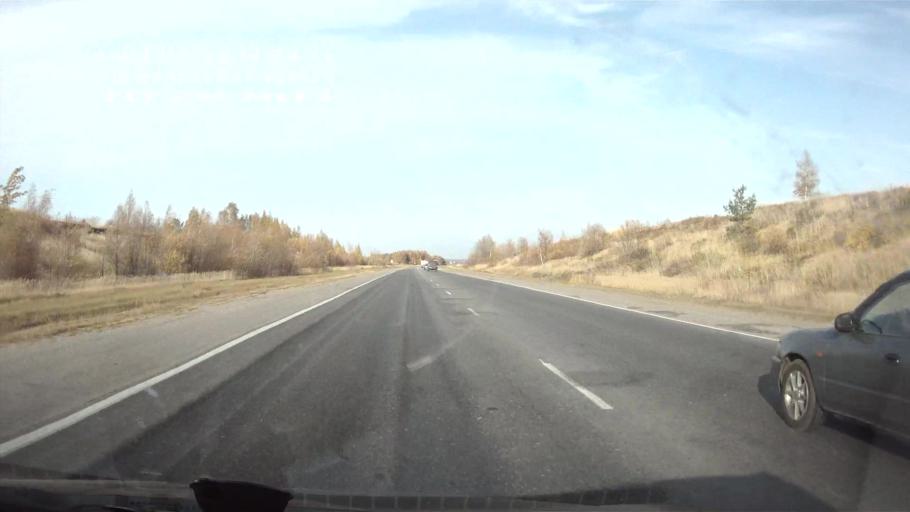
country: RU
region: Chuvashia
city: Kugesi
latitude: 56.0428
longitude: 47.3669
